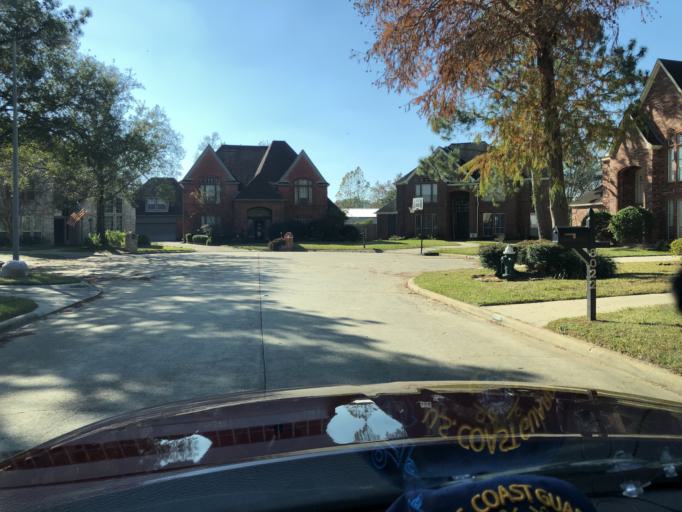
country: US
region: Texas
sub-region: Harris County
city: Tomball
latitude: 30.0314
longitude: -95.5472
